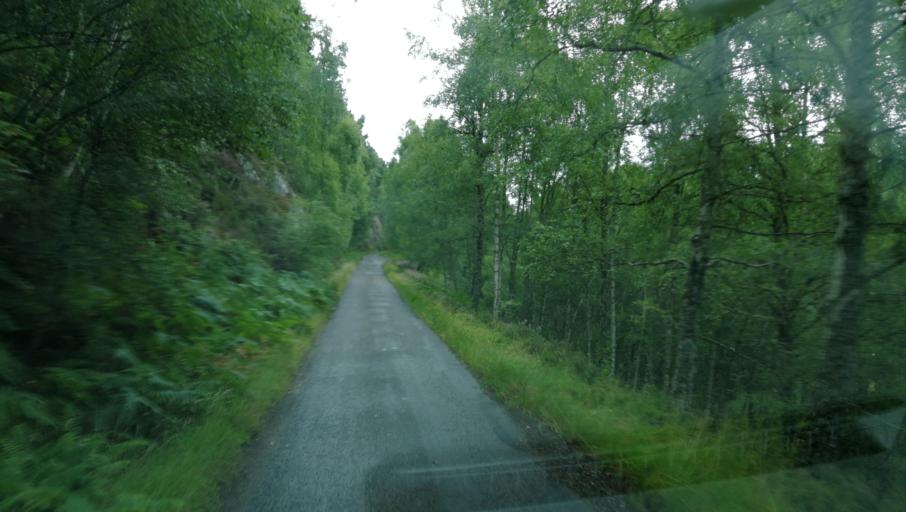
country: GB
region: Scotland
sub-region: Highland
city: Spean Bridge
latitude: 57.2953
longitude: -4.9132
